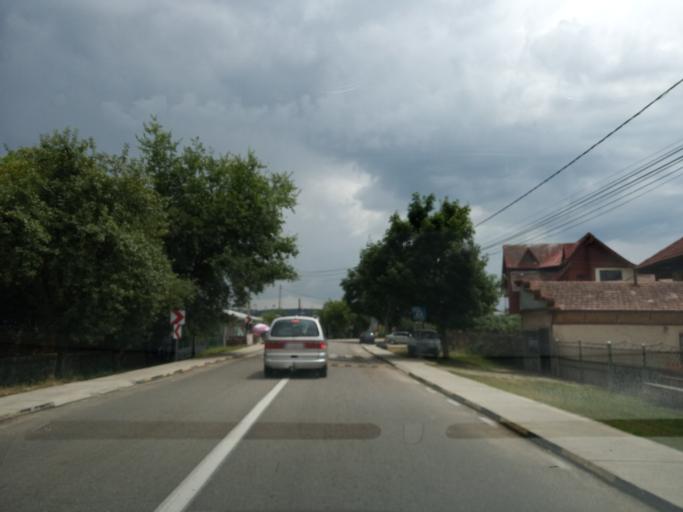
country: RO
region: Gorj
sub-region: Comuna Tismana
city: Tismana
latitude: 45.0435
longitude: 22.9515
